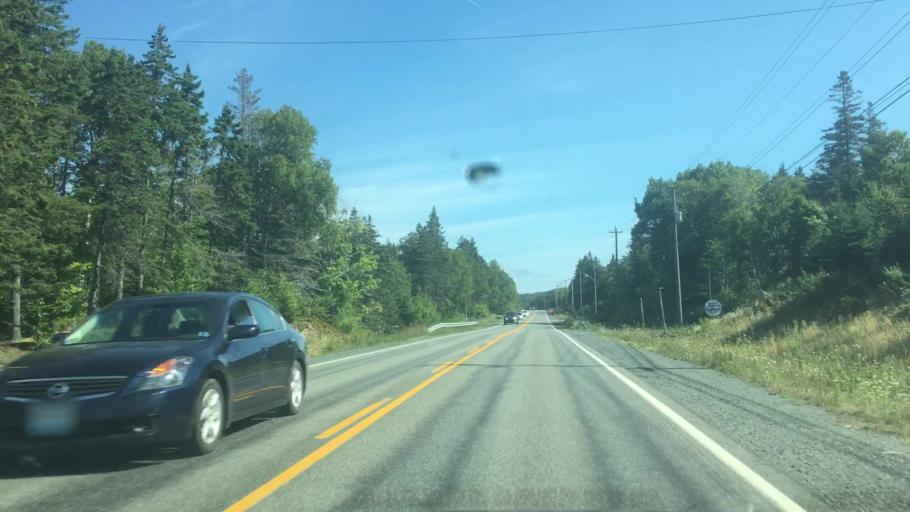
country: CA
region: Nova Scotia
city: Sydney
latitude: 45.9858
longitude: -60.4194
